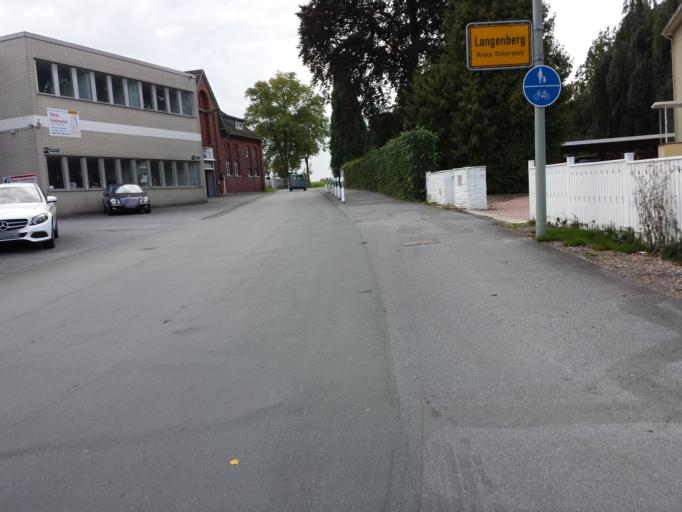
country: DE
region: North Rhine-Westphalia
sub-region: Regierungsbezirk Detmold
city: Langenberg
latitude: 51.7868
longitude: 8.3205
